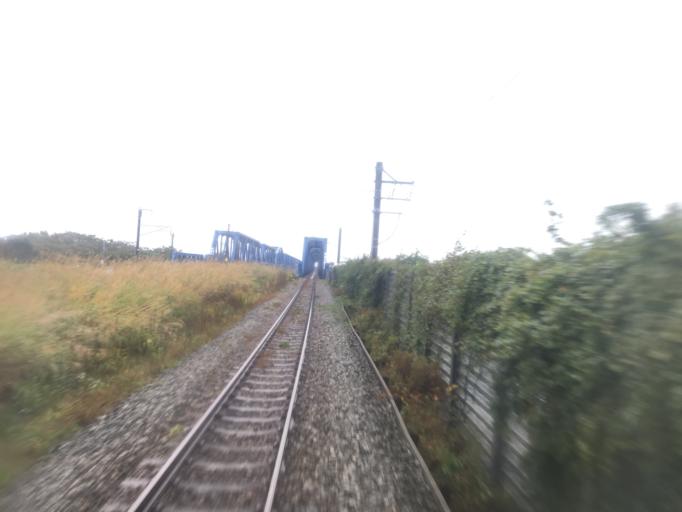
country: JP
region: Yamagata
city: Sakata
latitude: 38.8822
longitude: 139.9091
